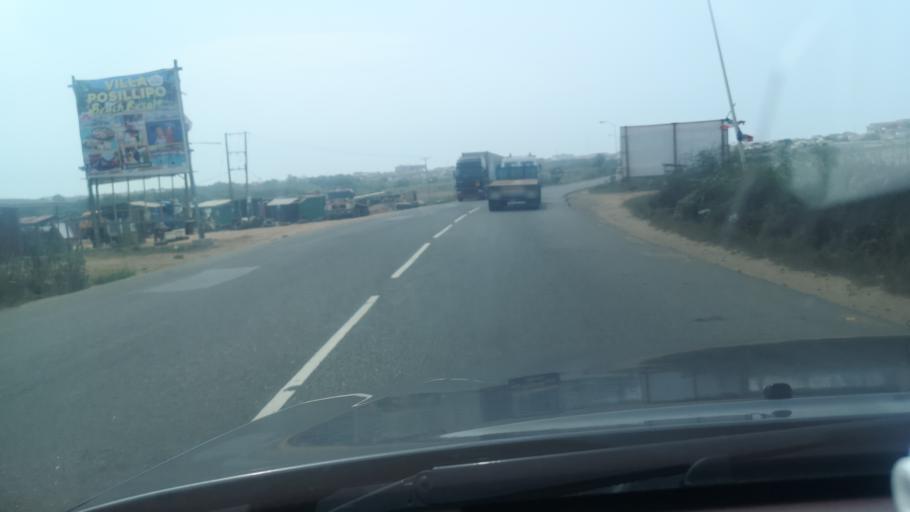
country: GH
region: Greater Accra
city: Nungua
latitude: 5.6108
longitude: -0.0530
